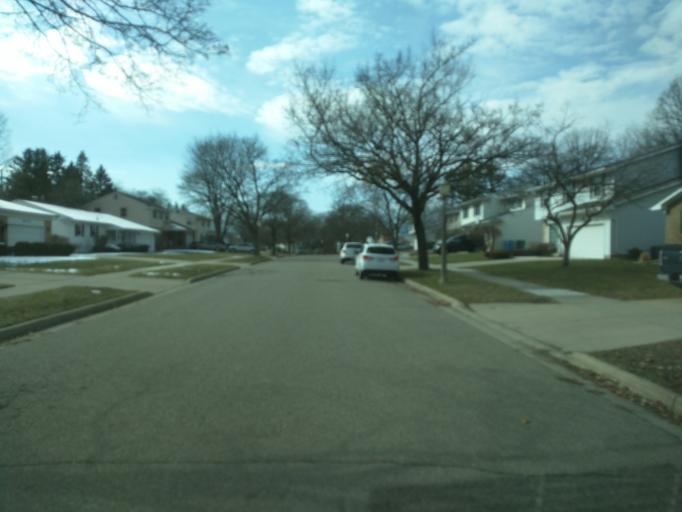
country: US
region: Michigan
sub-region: Ingham County
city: Edgemont Park
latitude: 42.7067
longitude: -84.5971
